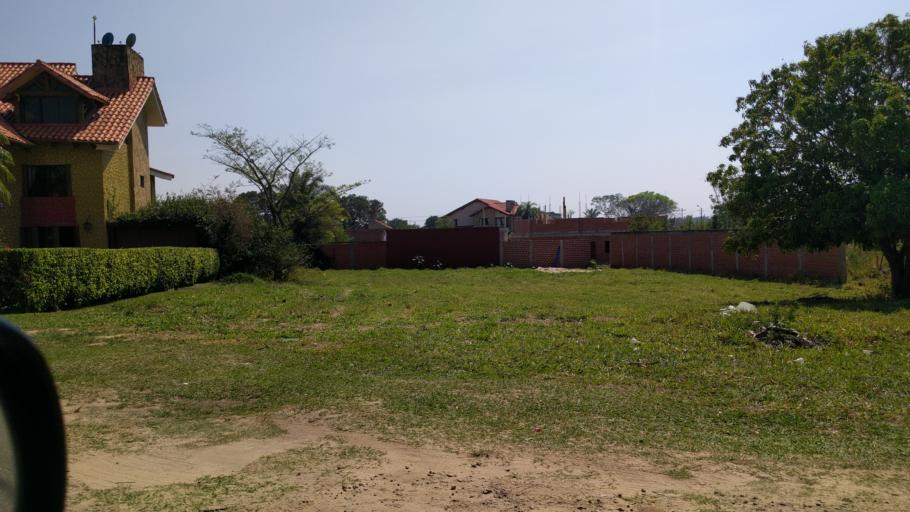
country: BO
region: Santa Cruz
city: Santa Cruz de la Sierra
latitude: -17.7537
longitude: -63.2277
